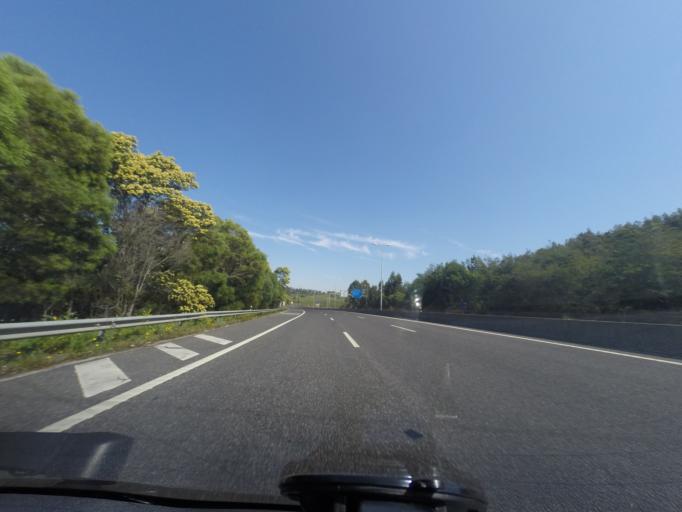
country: PT
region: Lisbon
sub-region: Odivelas
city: Canecas
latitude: 38.7891
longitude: -9.2370
